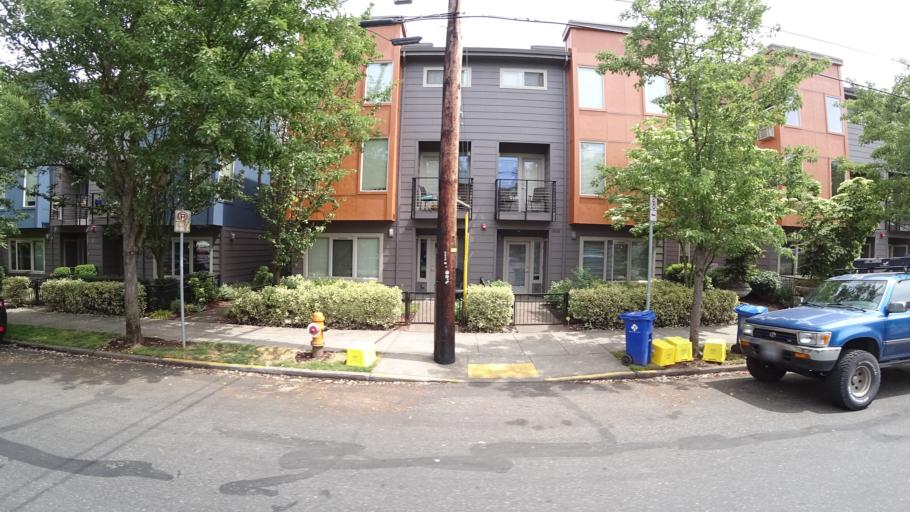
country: US
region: Oregon
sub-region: Washington County
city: West Haven
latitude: 45.5916
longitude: -122.7539
